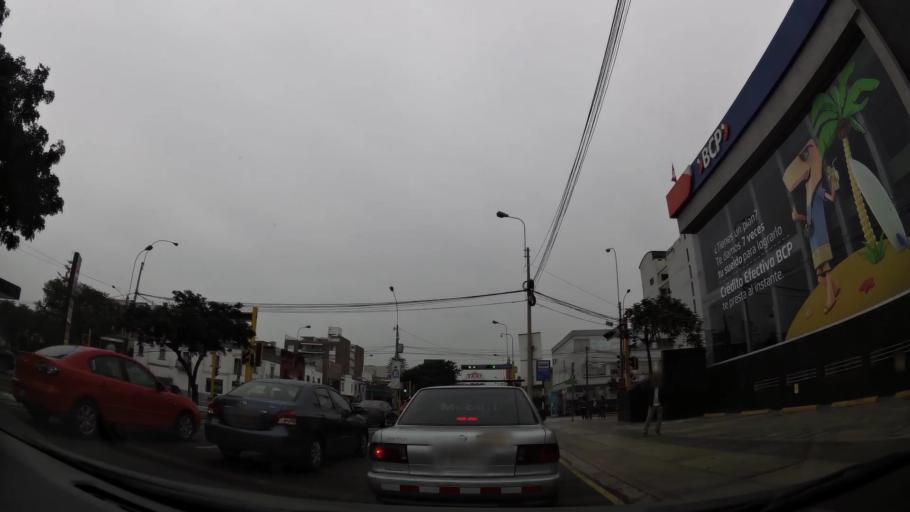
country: PE
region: Lima
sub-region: Lima
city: San Isidro
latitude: -12.1143
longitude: -77.0368
